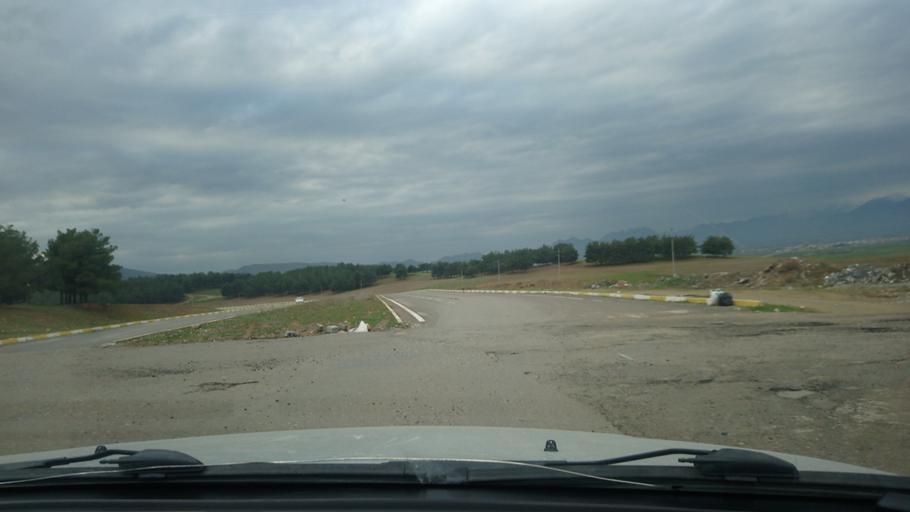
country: IQ
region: As Sulaymaniyah
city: Qeladize
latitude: 36.2002
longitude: 45.1108
